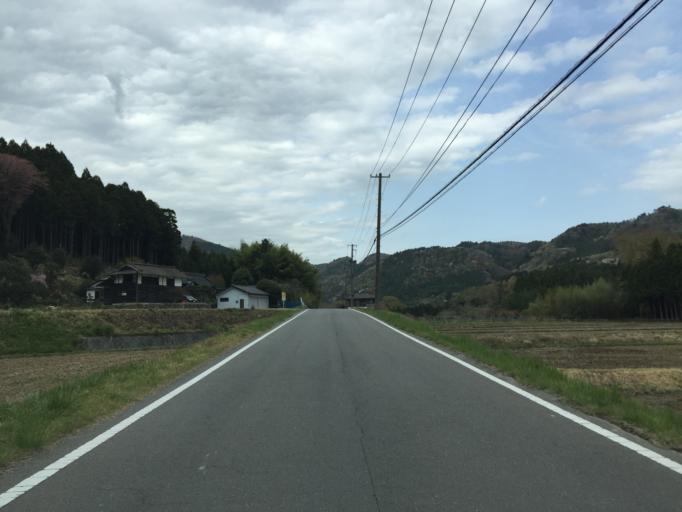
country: JP
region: Fukushima
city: Iwaki
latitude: 37.1302
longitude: 140.9019
